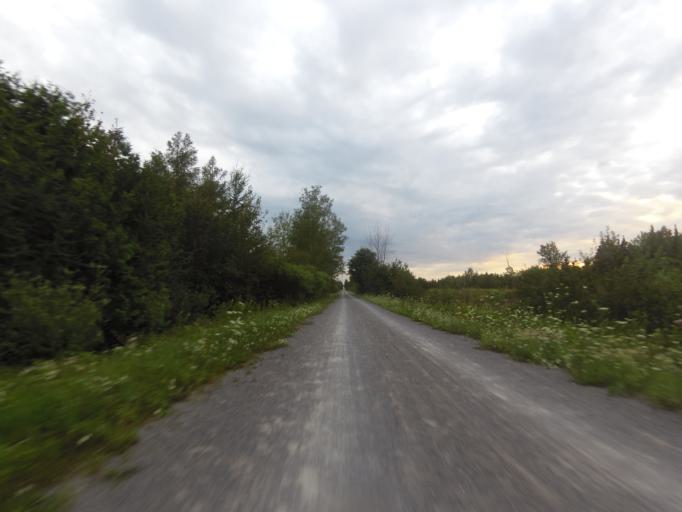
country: CA
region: Ontario
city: Carleton Place
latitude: 45.2020
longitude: -76.0099
